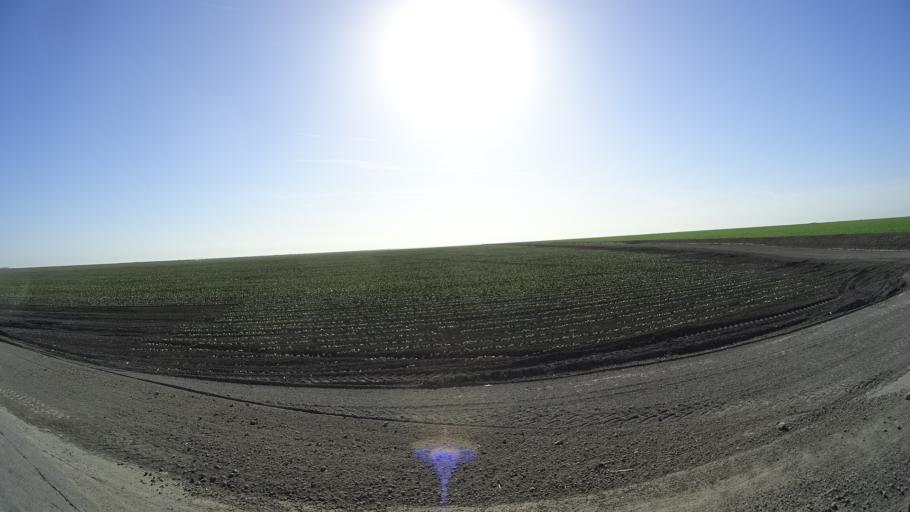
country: US
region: California
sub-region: Kings County
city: Stratford
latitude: 36.1091
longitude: -119.7980
